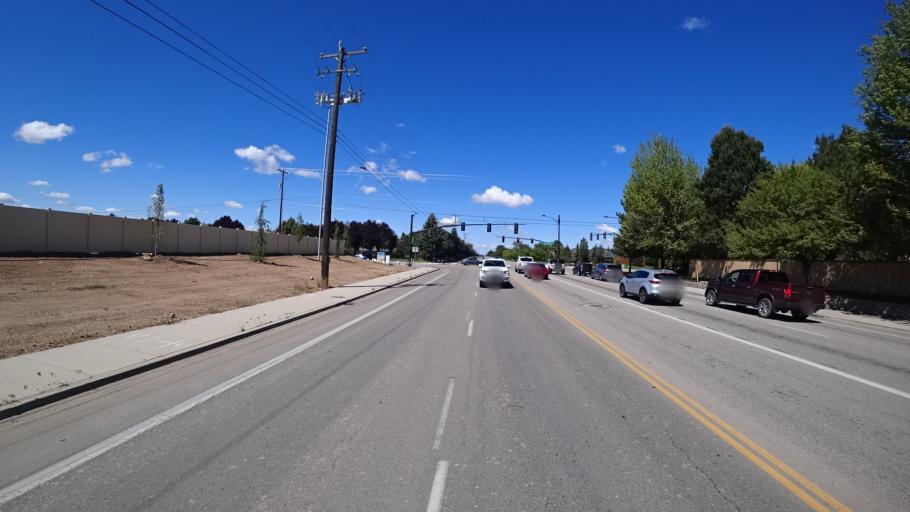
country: US
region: Idaho
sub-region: Ada County
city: Meridian
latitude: 43.6338
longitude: -116.3738
